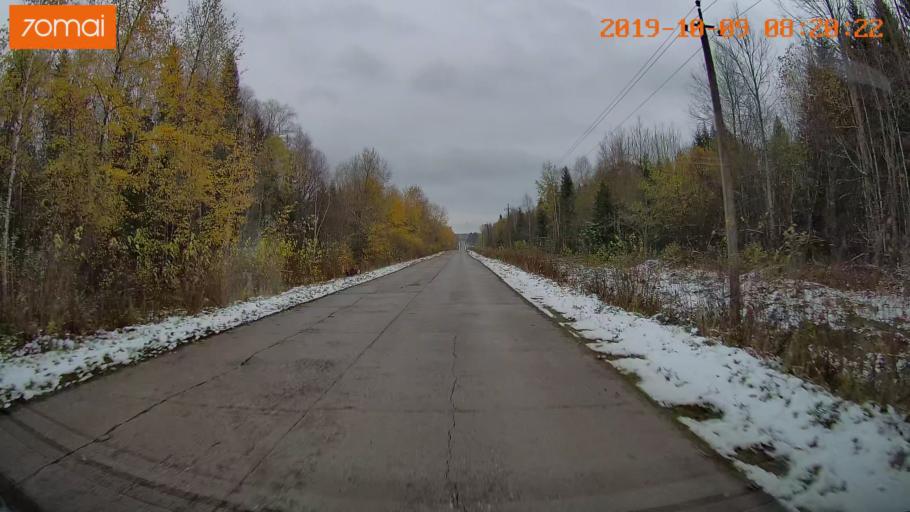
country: RU
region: Vologda
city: Gryazovets
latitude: 58.7428
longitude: 40.2584
